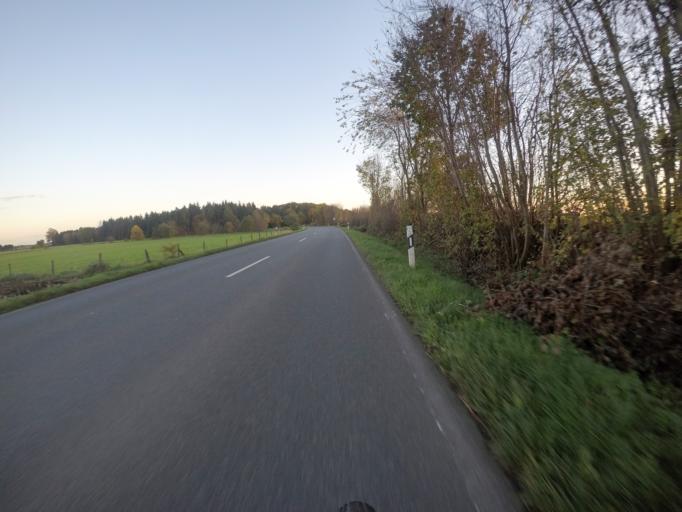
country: DE
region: North Rhine-Westphalia
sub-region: Regierungsbezirk Munster
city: Isselburg
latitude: 51.8469
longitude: 6.4775
